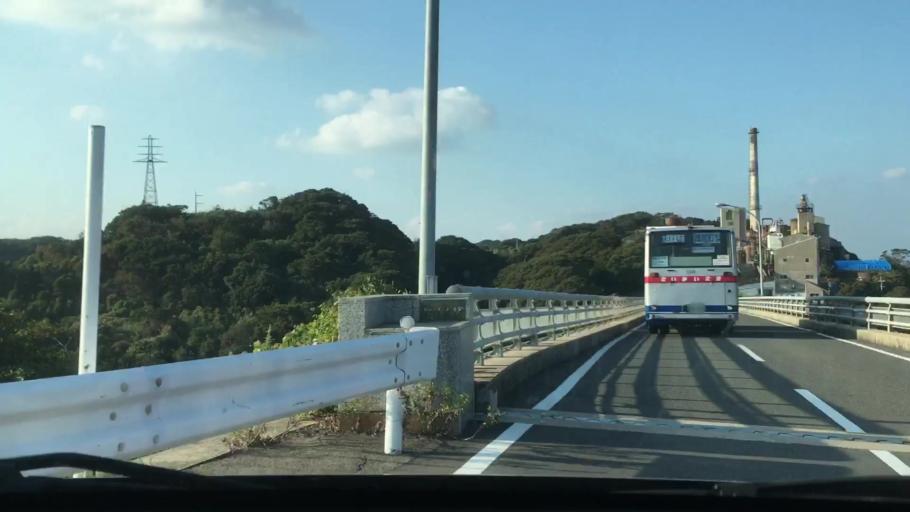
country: JP
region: Nagasaki
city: Sasebo
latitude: 33.0219
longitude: 129.5723
